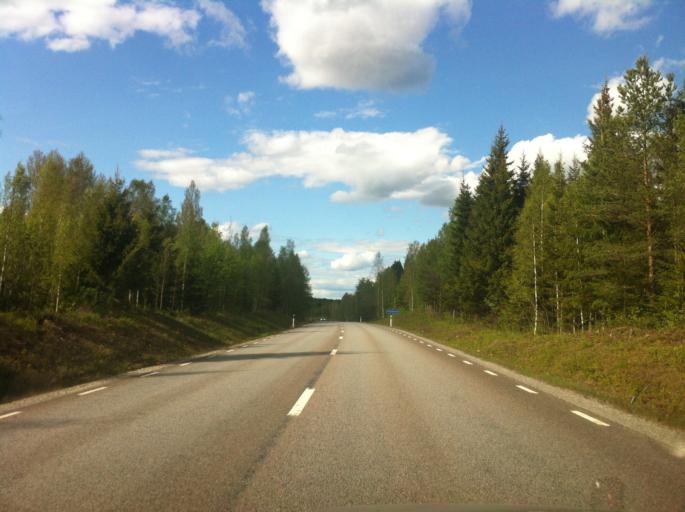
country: SE
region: Vaermland
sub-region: Filipstads Kommun
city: Filipstad
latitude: 59.7318
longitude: 14.2190
